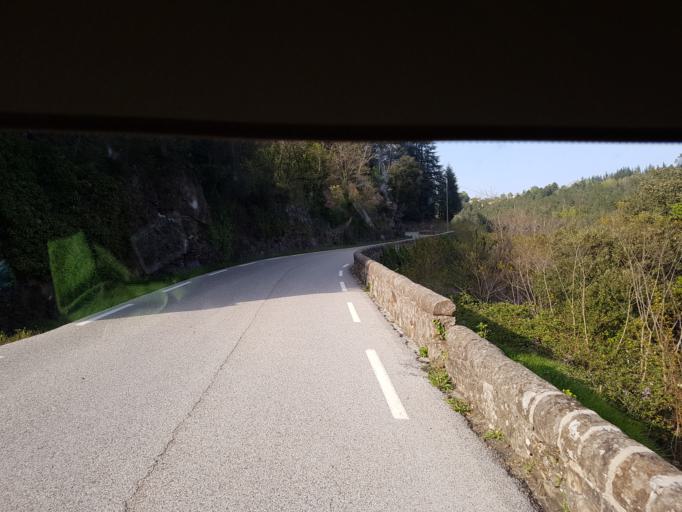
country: FR
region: Languedoc-Roussillon
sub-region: Departement du Gard
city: Branoux-les-Taillades
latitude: 44.3415
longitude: 3.9490
